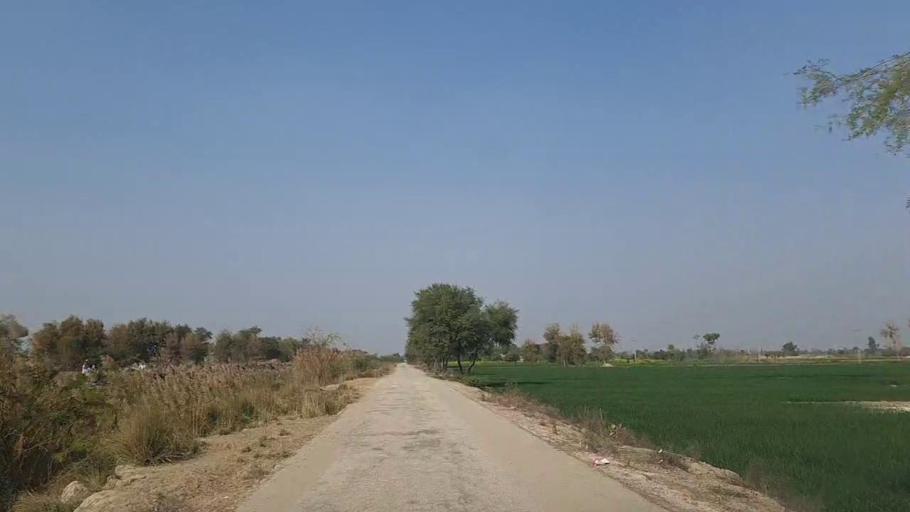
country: PK
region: Sindh
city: Daur
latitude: 26.4766
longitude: 68.4655
